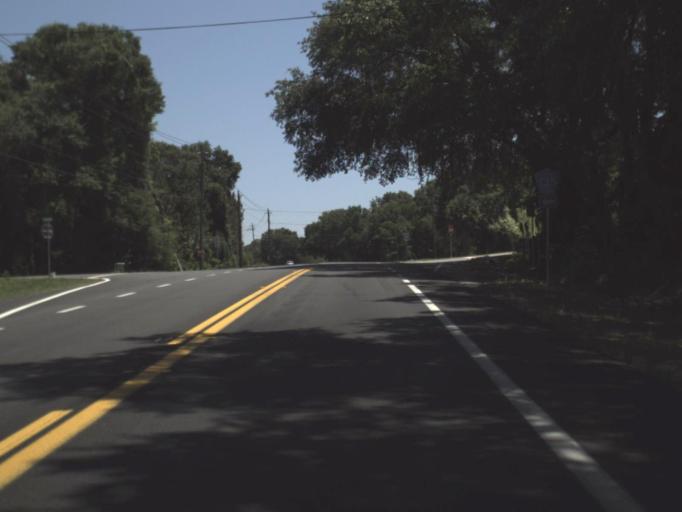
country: US
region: Florida
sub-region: Suwannee County
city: Wellborn
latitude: 30.1961
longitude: -82.7590
